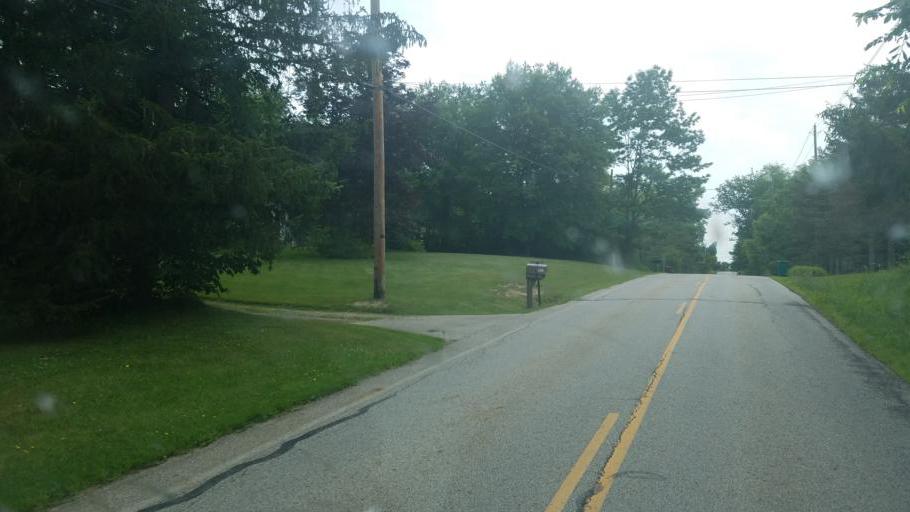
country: US
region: Ohio
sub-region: Geauga County
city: Burton
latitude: 41.4806
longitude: -81.2255
